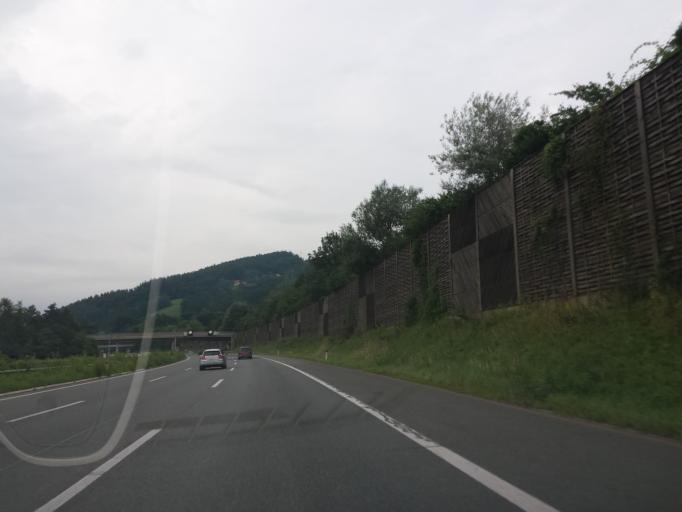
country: AT
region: Styria
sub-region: Politischer Bezirk Graz-Umgebung
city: Deutschfeistritz
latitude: 47.1662
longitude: 15.3313
